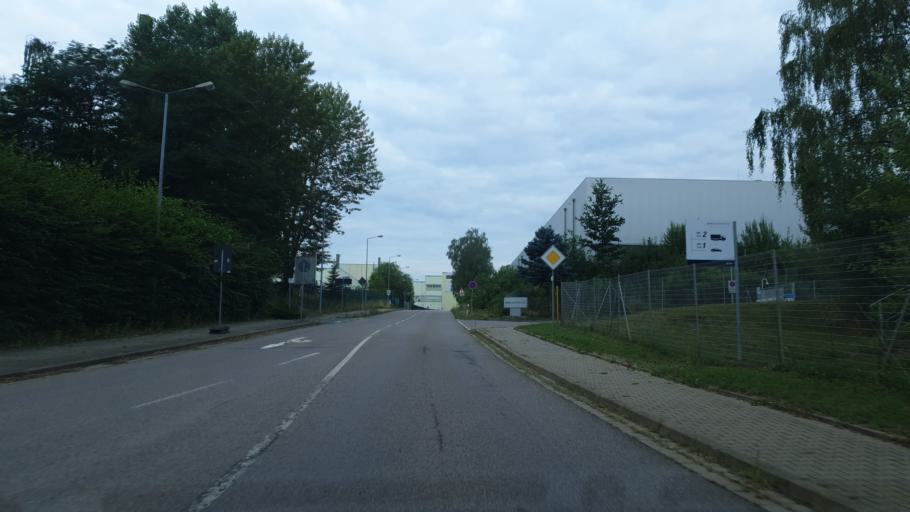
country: DE
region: Saxony
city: Sankt Egidien
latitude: 50.7919
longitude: 12.6259
